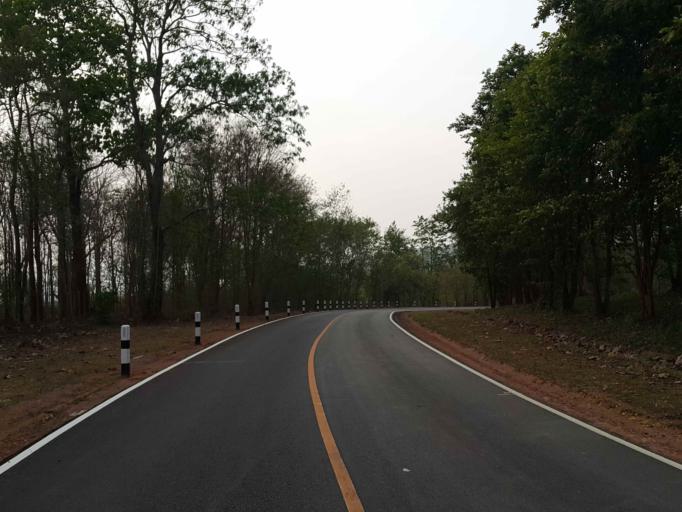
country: TH
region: Chiang Mai
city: Mae Taeng
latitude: 19.1673
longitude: 99.0306
